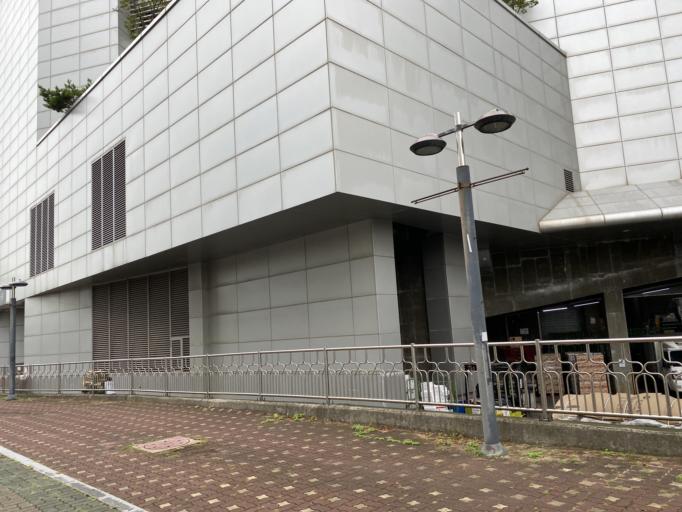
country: KR
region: Incheon
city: Incheon
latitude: 37.4927
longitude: 126.4922
